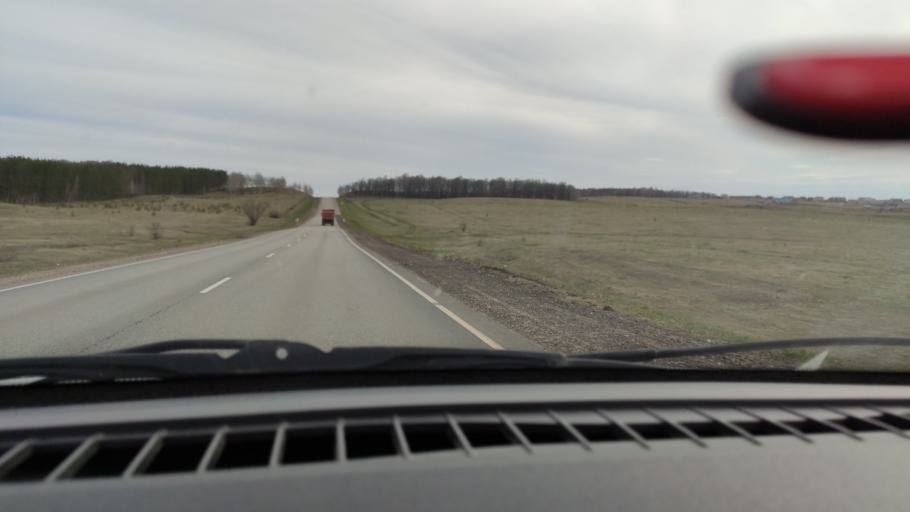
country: RU
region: Bashkortostan
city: Yermolayevo
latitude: 52.7164
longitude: 55.8556
